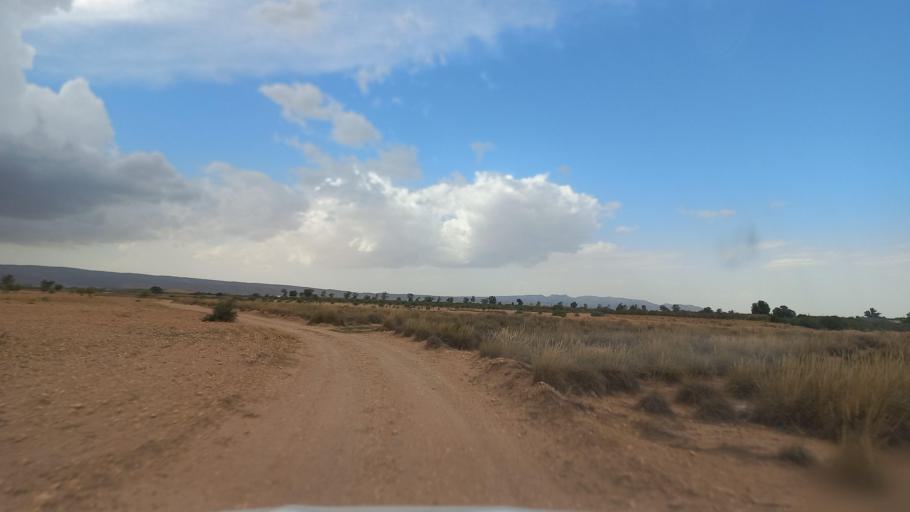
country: TN
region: Al Qasrayn
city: Kasserine
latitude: 35.2431
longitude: 9.0088
